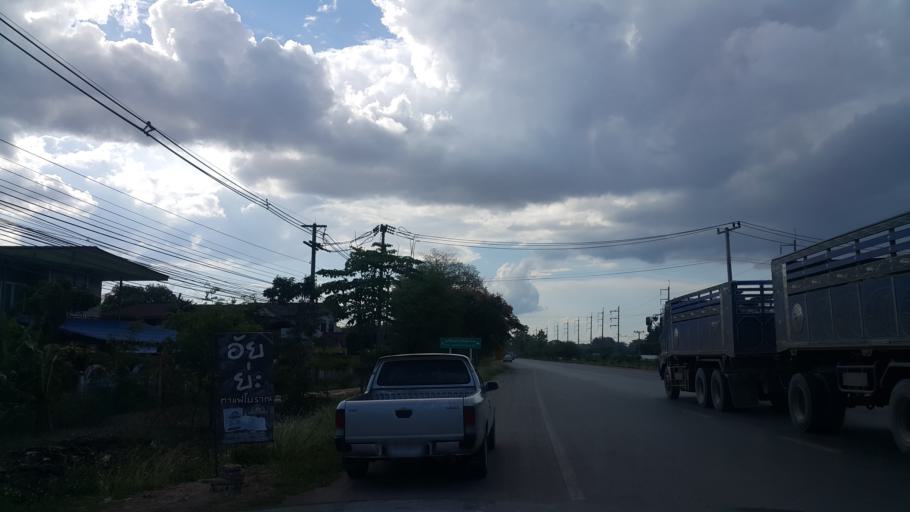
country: TH
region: Phayao
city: Dok Kham Tai
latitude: 19.0800
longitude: 99.9239
